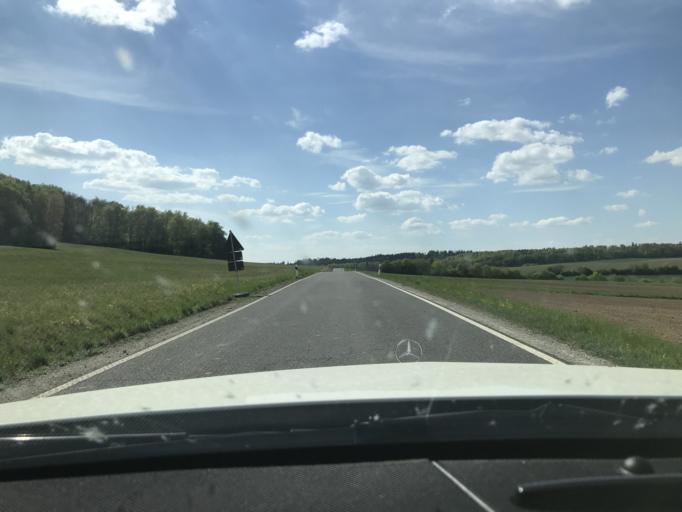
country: DE
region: Hesse
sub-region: Regierungsbezirk Kassel
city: Weissenborn
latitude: 51.1200
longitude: 10.0802
